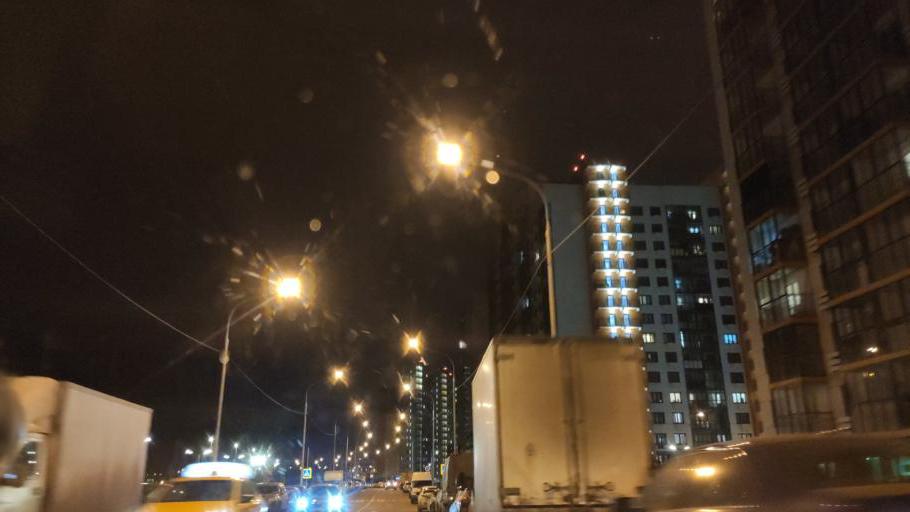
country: RU
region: Moscow
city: Annino
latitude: 55.5333
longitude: 37.6212
